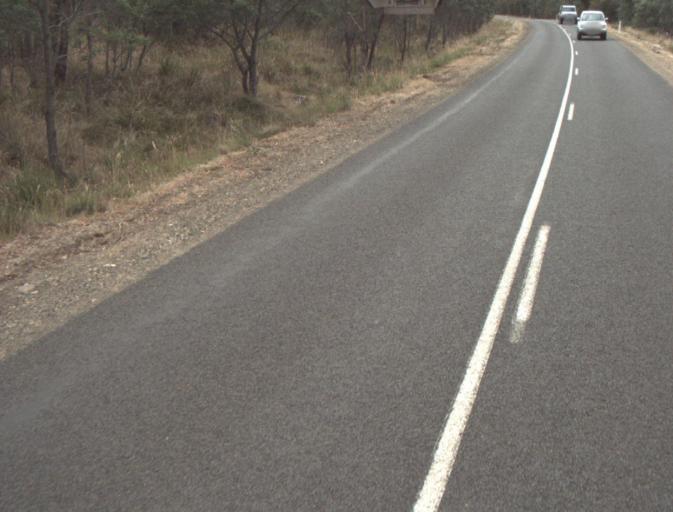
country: AU
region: Tasmania
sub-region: Northern Midlands
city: Evandale
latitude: -41.5100
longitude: 147.3465
